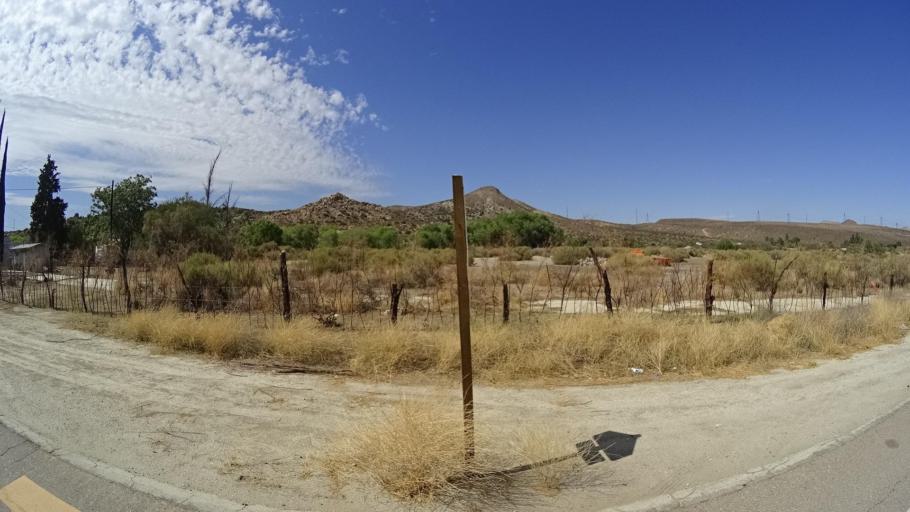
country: MX
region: Baja California
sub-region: Tecate
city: Cereso del Hongo
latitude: 32.6154
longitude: -116.1937
